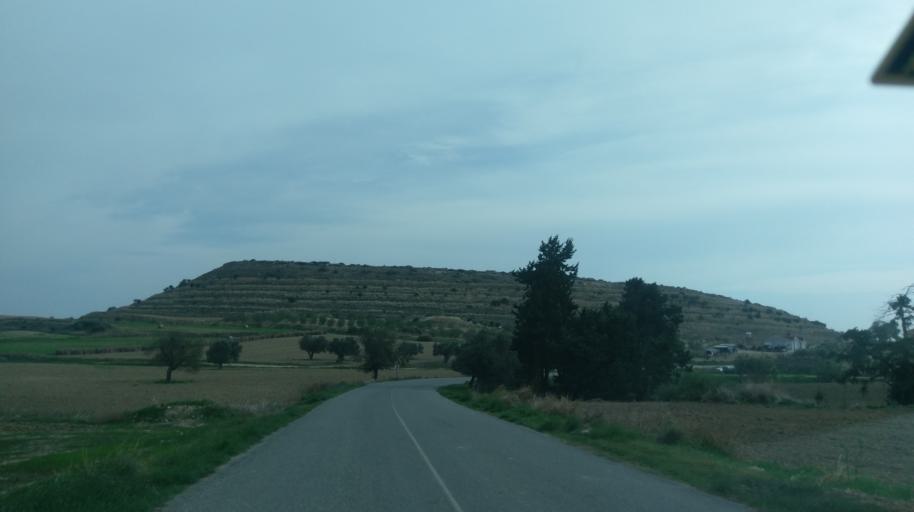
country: CY
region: Ammochostos
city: Trikomo
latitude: 35.3309
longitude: 33.9319
